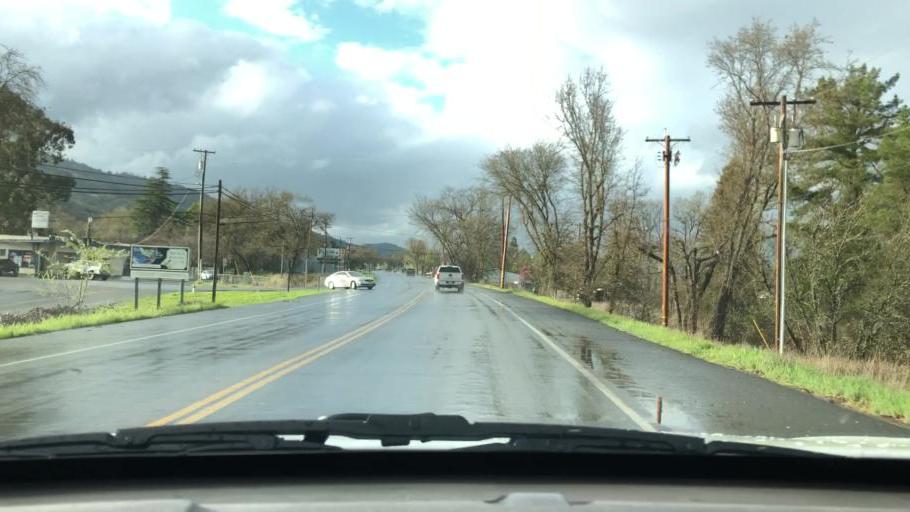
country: US
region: California
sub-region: Mendocino County
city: Ukiah
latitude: 39.1168
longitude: -123.2000
